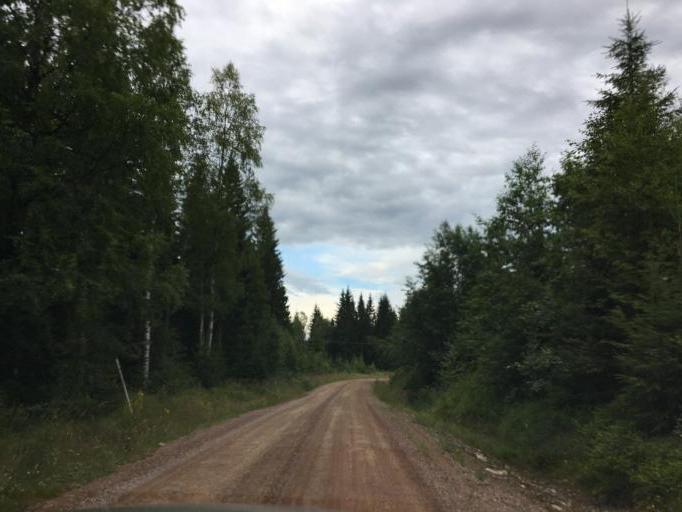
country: SE
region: Vaermland
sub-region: Filipstads Kommun
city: Lesjofors
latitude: 60.1916
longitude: 14.3987
